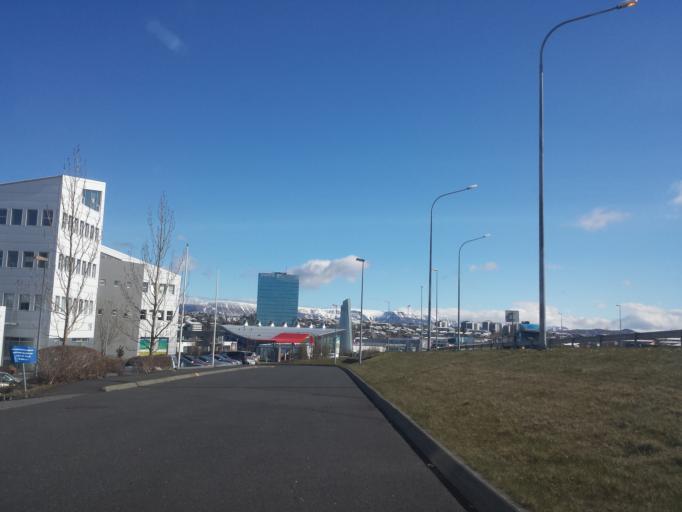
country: IS
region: Capital Region
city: Kopavogur
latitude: 64.0977
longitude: -21.8855
